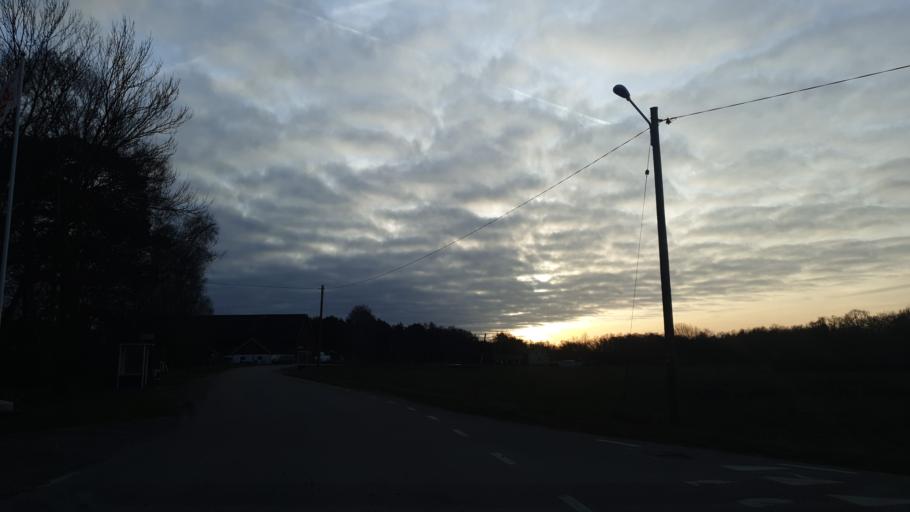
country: SE
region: Blekinge
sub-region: Karlskrona Kommun
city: Jaemjoe
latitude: 56.1507
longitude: 15.9025
